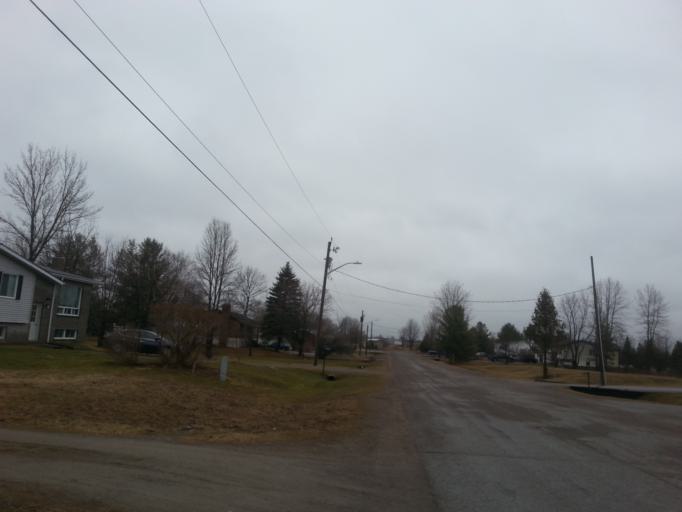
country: CA
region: Ontario
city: Orillia
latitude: 44.5500
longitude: -79.1763
